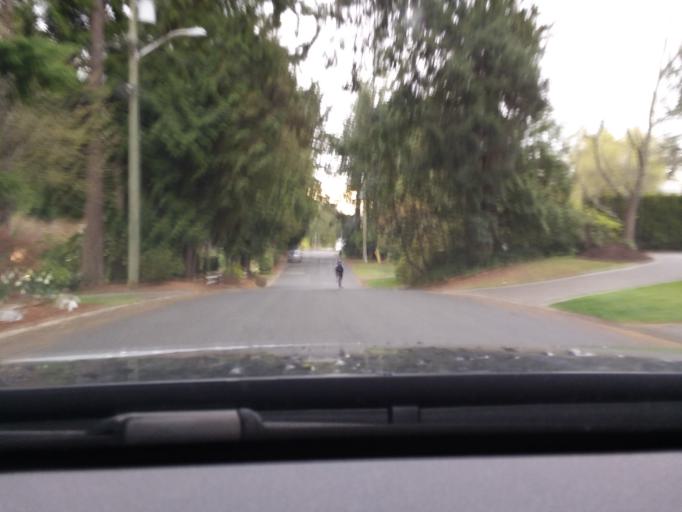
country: CA
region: British Columbia
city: Victoria
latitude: 48.5231
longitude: -123.3816
